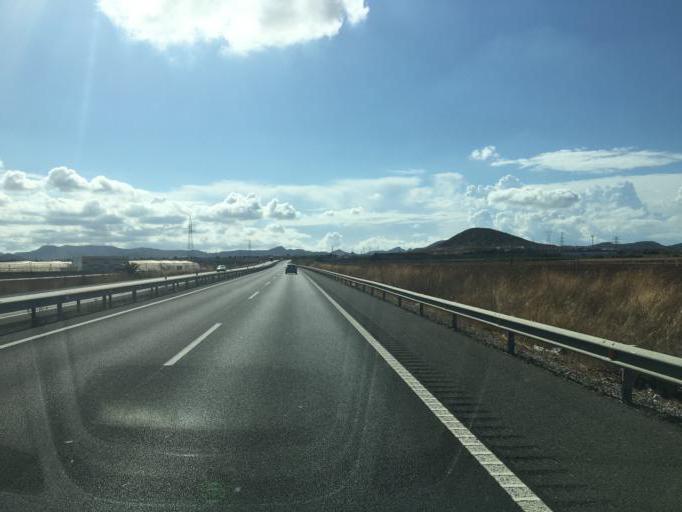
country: ES
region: Murcia
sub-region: Murcia
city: Cartagena
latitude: 37.6438
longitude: -0.9669
